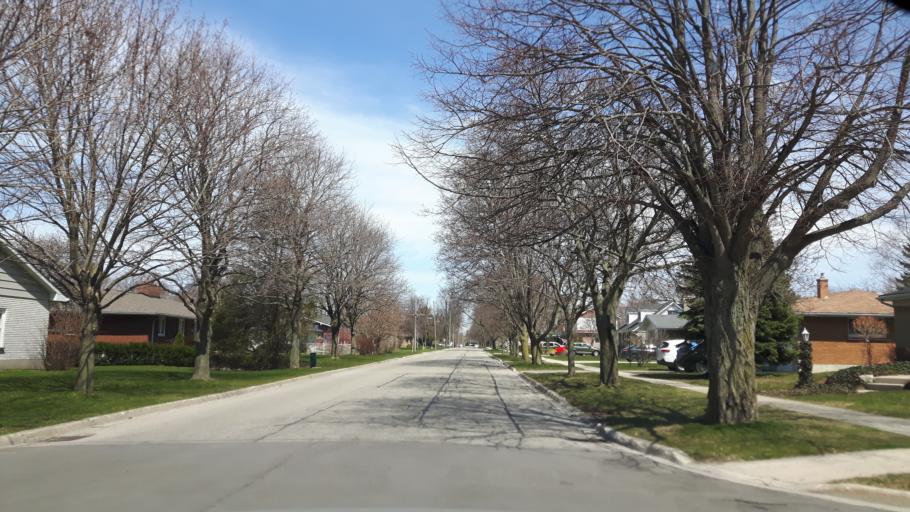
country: CA
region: Ontario
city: Goderich
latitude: 43.7336
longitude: -81.7215
